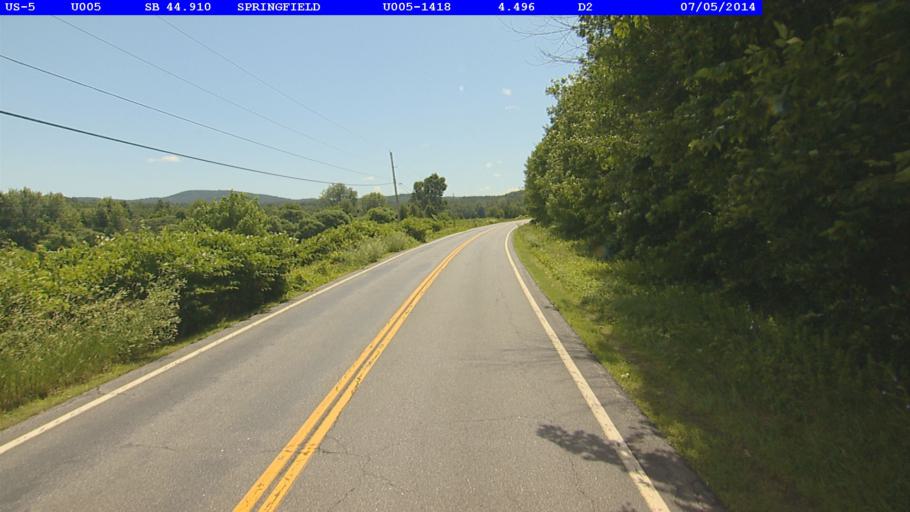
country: US
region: New Hampshire
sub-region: Sullivan County
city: Charlestown
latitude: 43.2784
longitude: -72.4133
